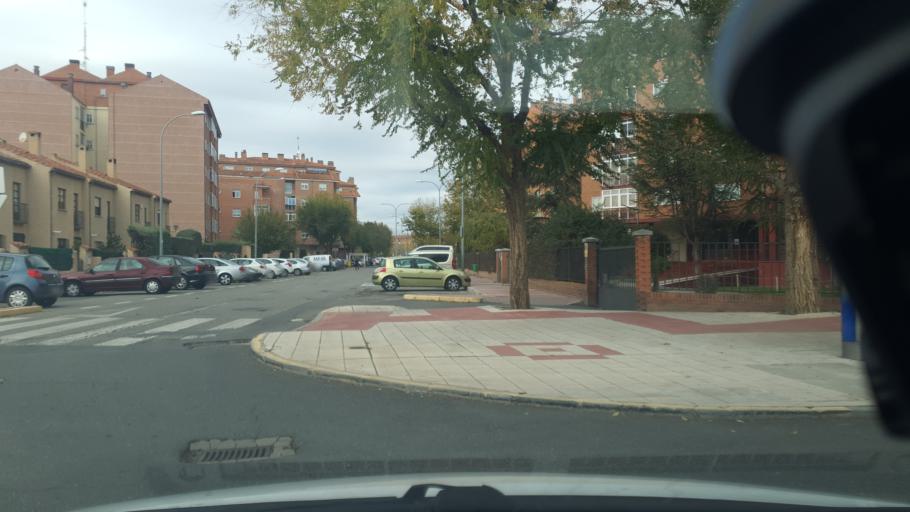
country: ES
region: Castille and Leon
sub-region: Provincia de Avila
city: Avila
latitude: 40.6461
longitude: -4.6831
